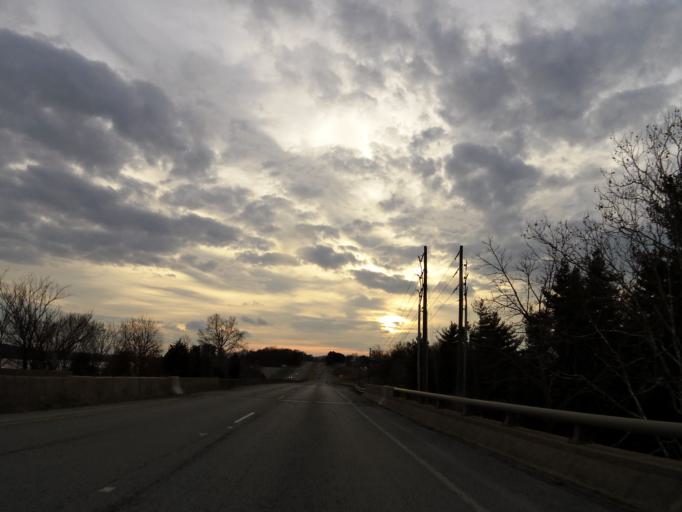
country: US
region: Tennessee
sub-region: Monroe County
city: Vonore
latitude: 35.6038
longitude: -84.2142
